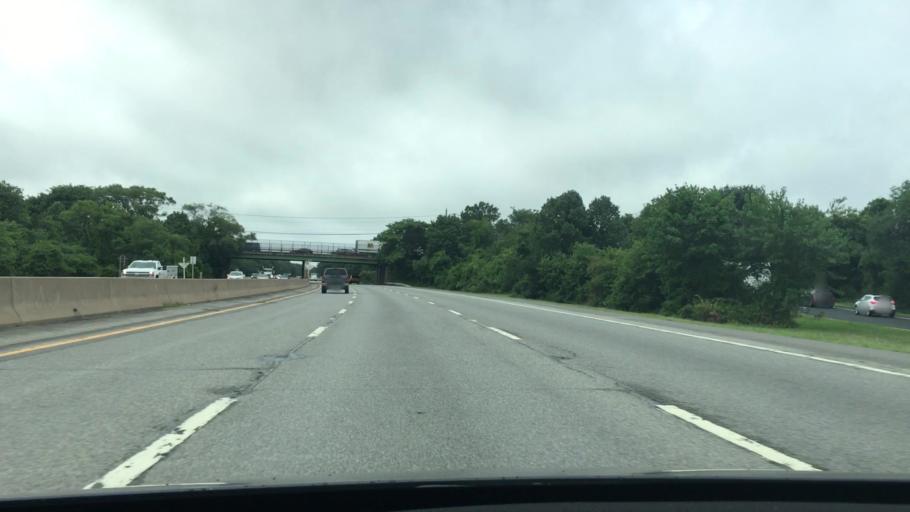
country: US
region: New York
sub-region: Nassau County
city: Plainview
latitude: 40.7755
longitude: -73.4819
